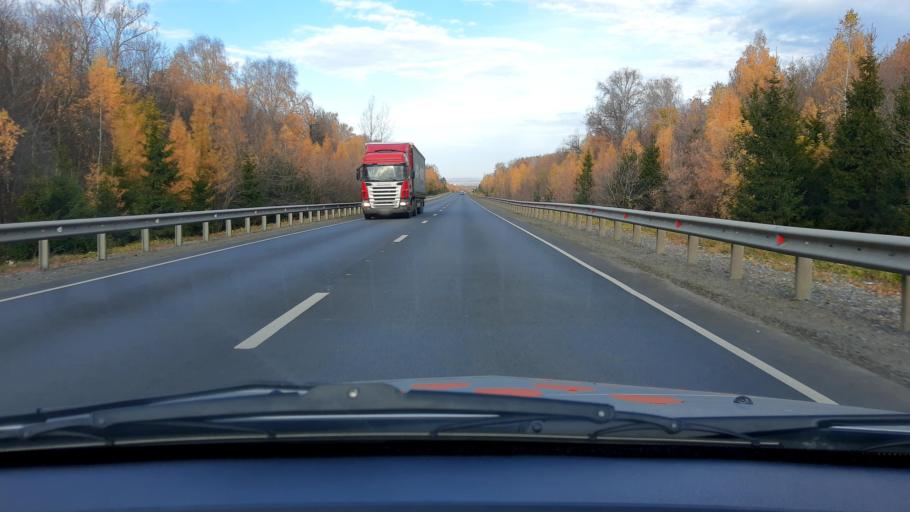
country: RU
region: Bashkortostan
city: Avdon
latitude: 54.8388
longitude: 55.7193
